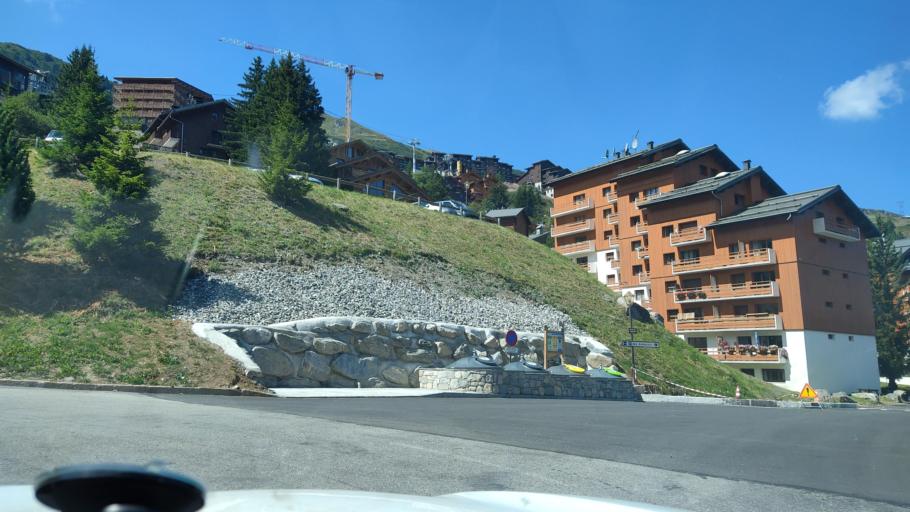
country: FR
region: Rhone-Alpes
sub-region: Departement de la Savoie
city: Meribel
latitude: 45.3750
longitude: 6.5775
